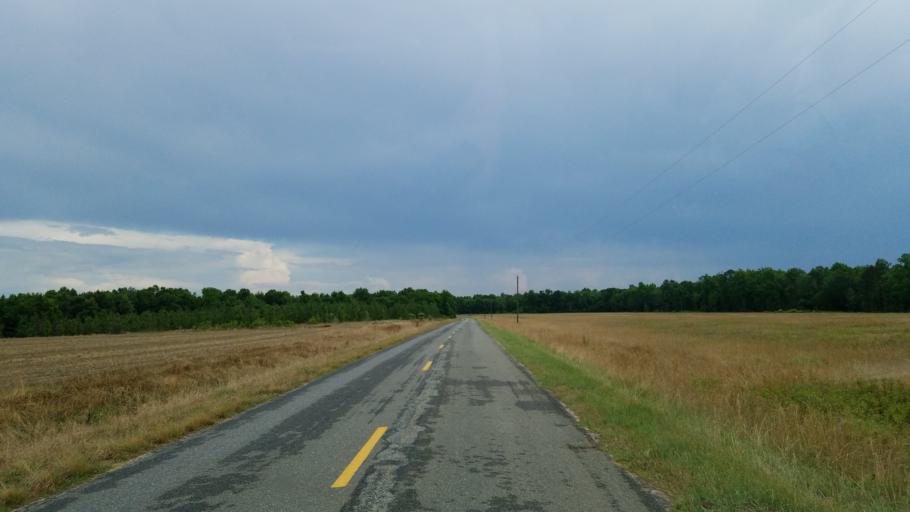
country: US
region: Georgia
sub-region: Dooly County
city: Unadilla
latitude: 32.2727
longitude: -83.7964
